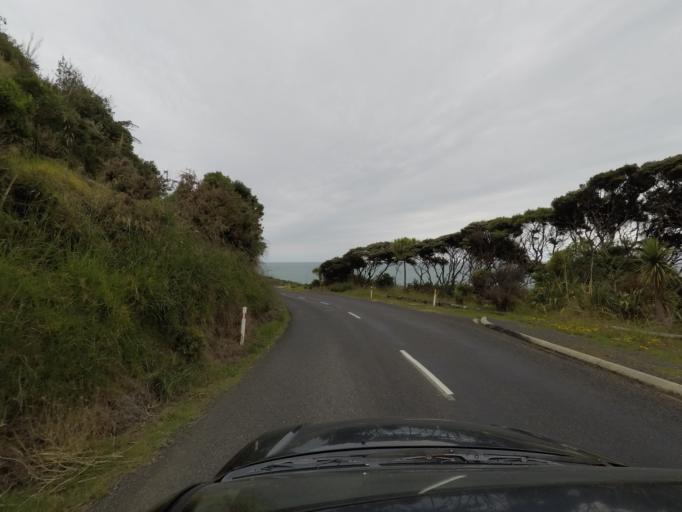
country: NZ
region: Waikato
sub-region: Waikato District
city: Raglan
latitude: -37.8233
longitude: 174.8130
